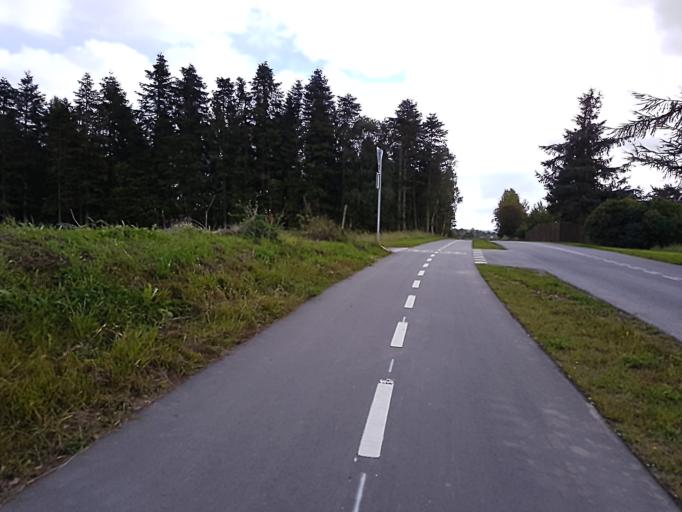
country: DK
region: Zealand
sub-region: Roskilde Kommune
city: Gundsomagle
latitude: 55.7475
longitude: 12.1421
